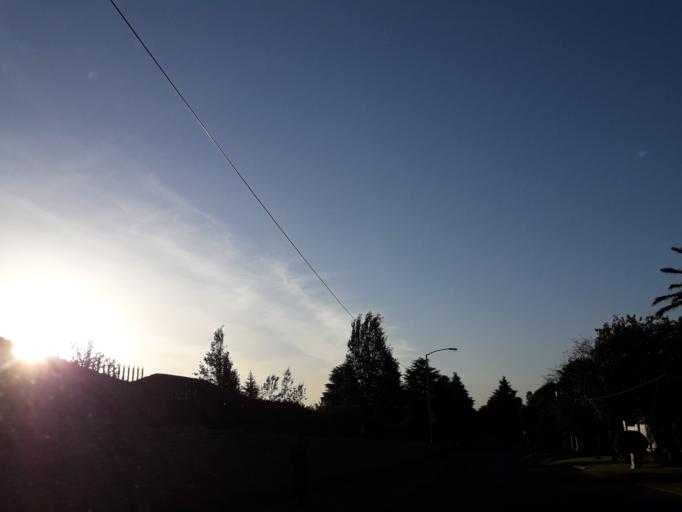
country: ZA
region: Gauteng
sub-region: City of Johannesburg Metropolitan Municipality
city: Roodepoort
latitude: -26.1613
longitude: 27.9500
